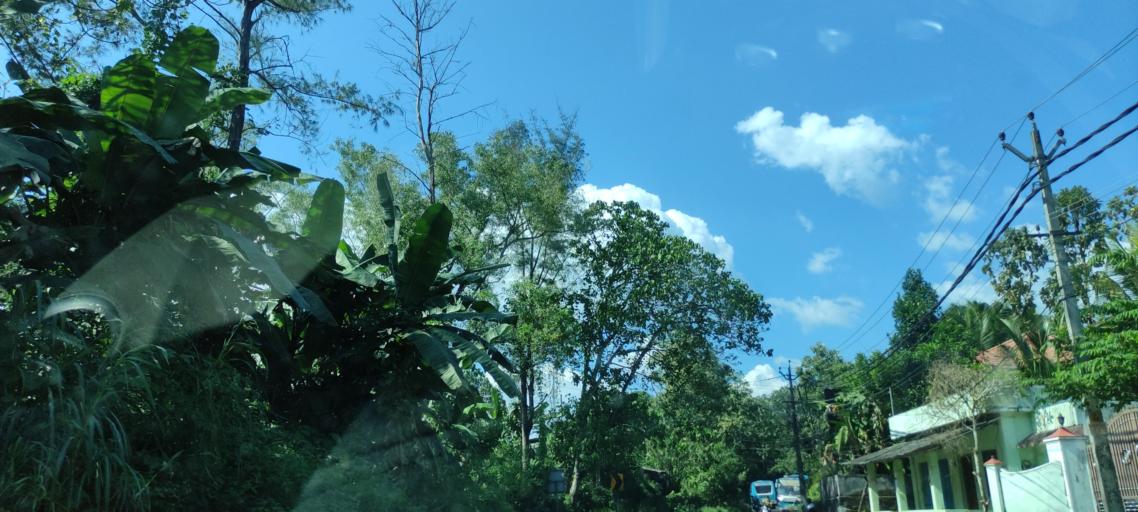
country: IN
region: Kerala
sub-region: Pattanamtitta
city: Adur
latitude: 9.1635
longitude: 76.7435
